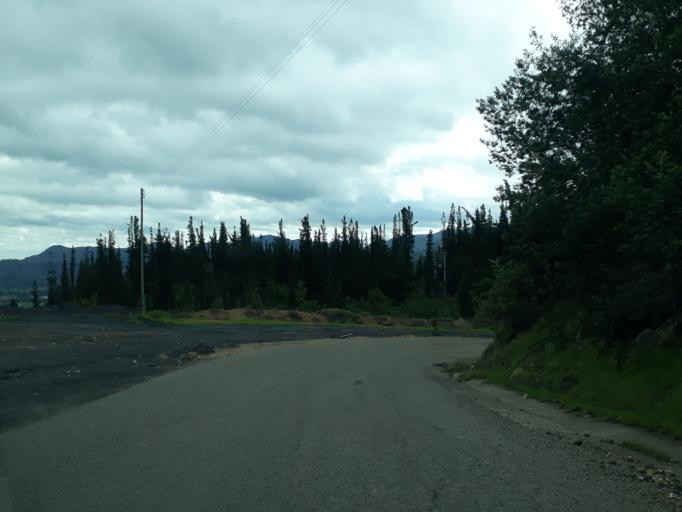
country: CO
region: Cundinamarca
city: Cucunuba
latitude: 5.2261
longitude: -73.7794
